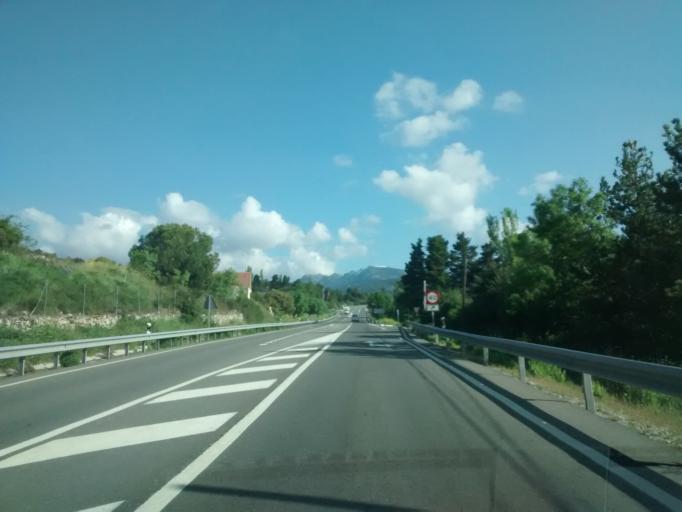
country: ES
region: Madrid
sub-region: Provincia de Madrid
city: Becerril de la Sierra
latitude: 40.7052
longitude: -4.0042
